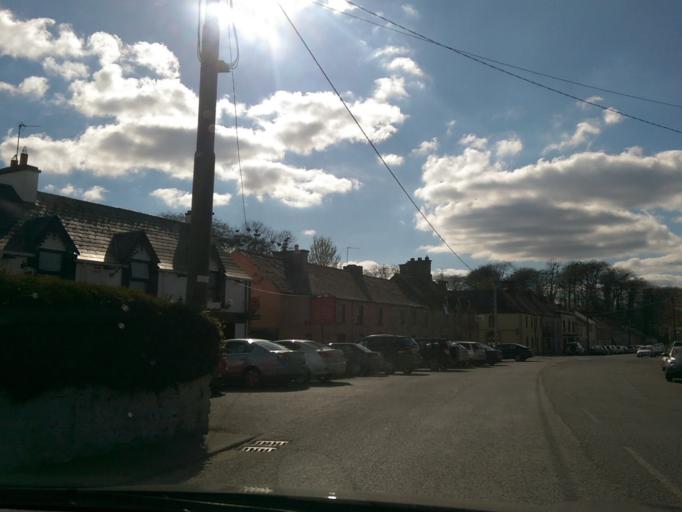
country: IE
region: Munster
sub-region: North Tipperary
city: Roscrea
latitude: 53.0978
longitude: -7.7203
